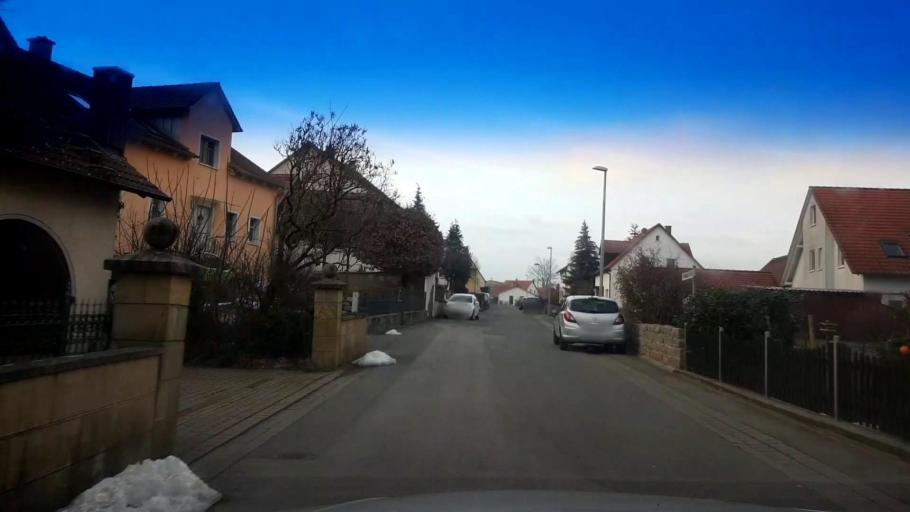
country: DE
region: Bavaria
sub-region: Upper Franconia
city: Hirschaid
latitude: 49.8038
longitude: 10.9877
